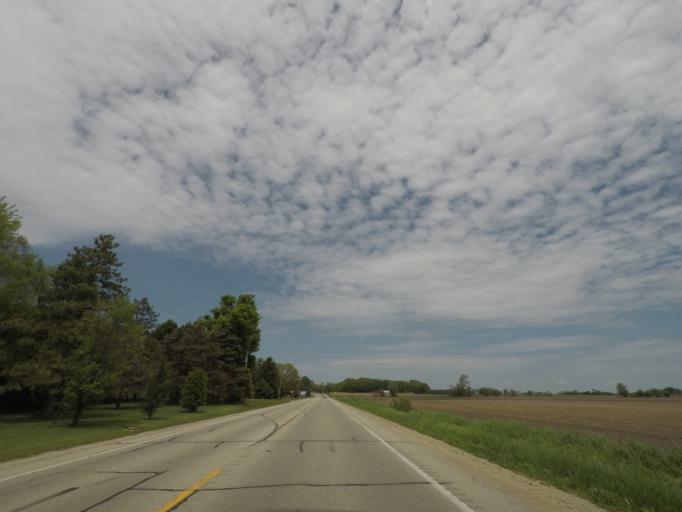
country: US
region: Wisconsin
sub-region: Rock County
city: Evansville
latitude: 42.8136
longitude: -89.2991
